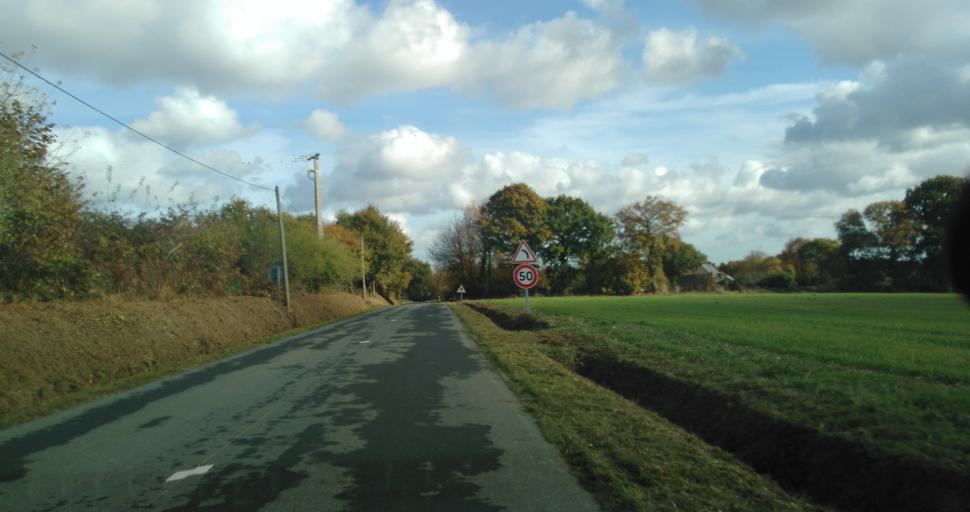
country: FR
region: Brittany
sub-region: Departement d'Ille-et-Vilaine
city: Boisgervilly
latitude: 48.1522
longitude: -2.0734
